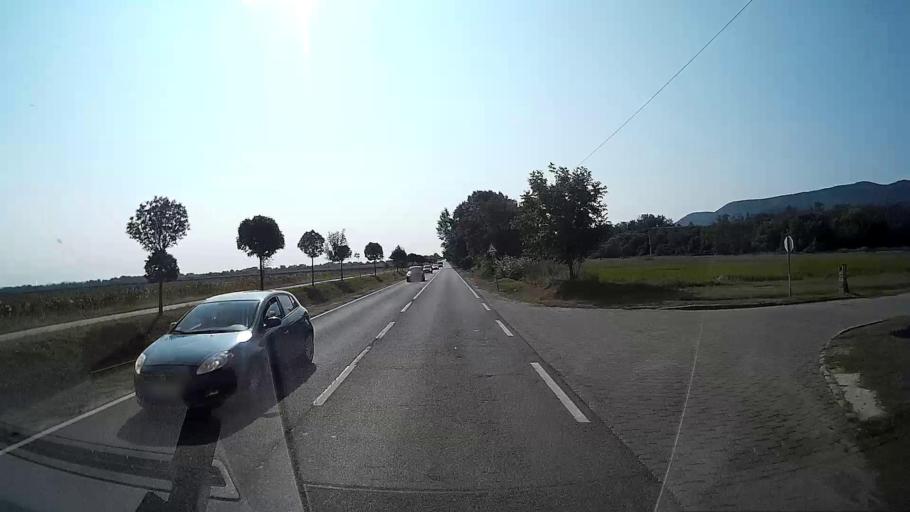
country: HU
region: Pest
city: Dunabogdany
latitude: 47.7792
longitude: 19.0517
